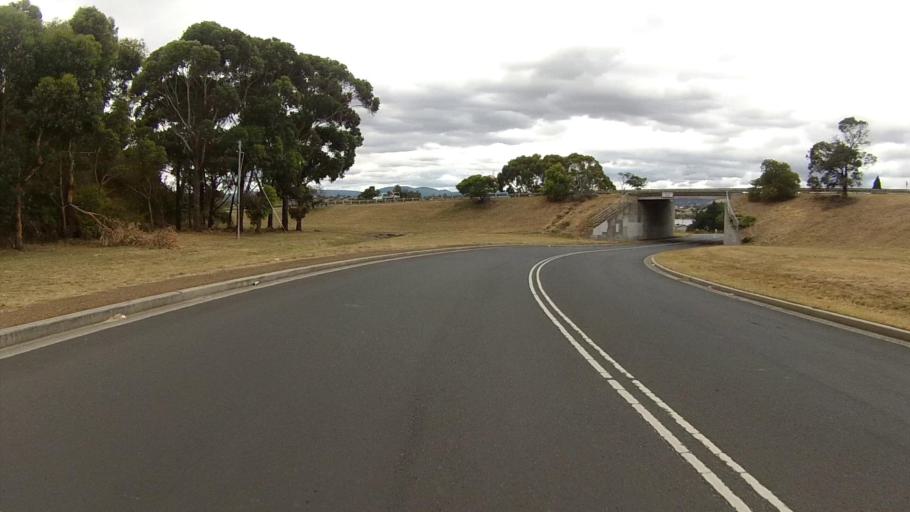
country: AU
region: Tasmania
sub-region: Glenorchy
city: Granton
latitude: -42.7530
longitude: 147.2281
